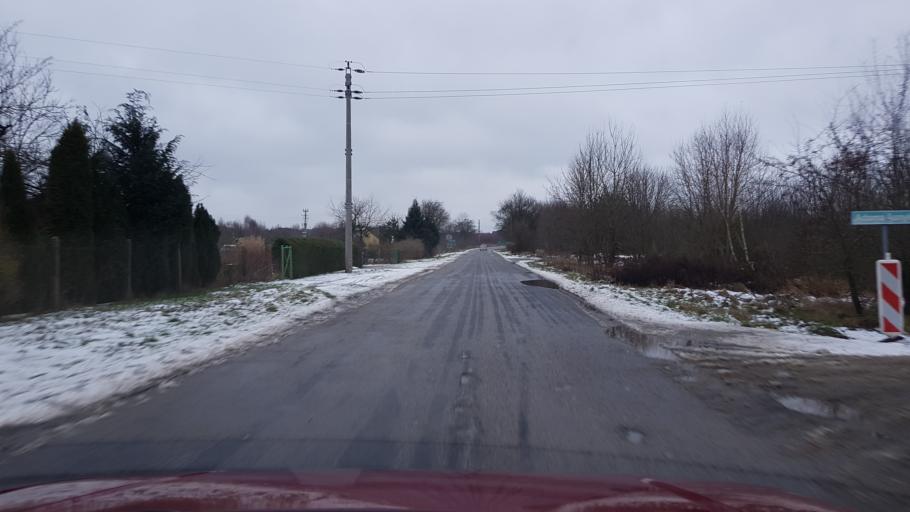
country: PL
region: West Pomeranian Voivodeship
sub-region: Powiat goleniowski
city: Nowogard
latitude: 53.6562
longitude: 15.1244
